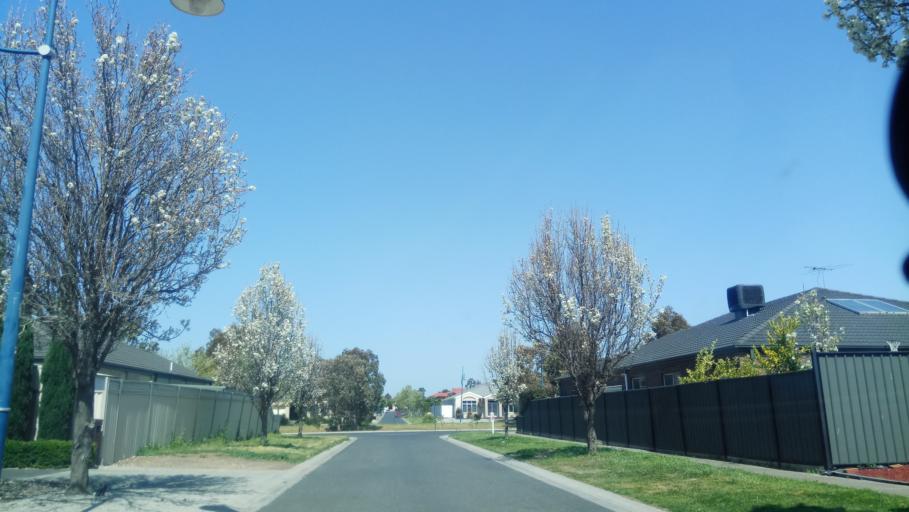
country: AU
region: Victoria
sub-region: Wyndham
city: Point Cook
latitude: -37.8939
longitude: 144.7379
